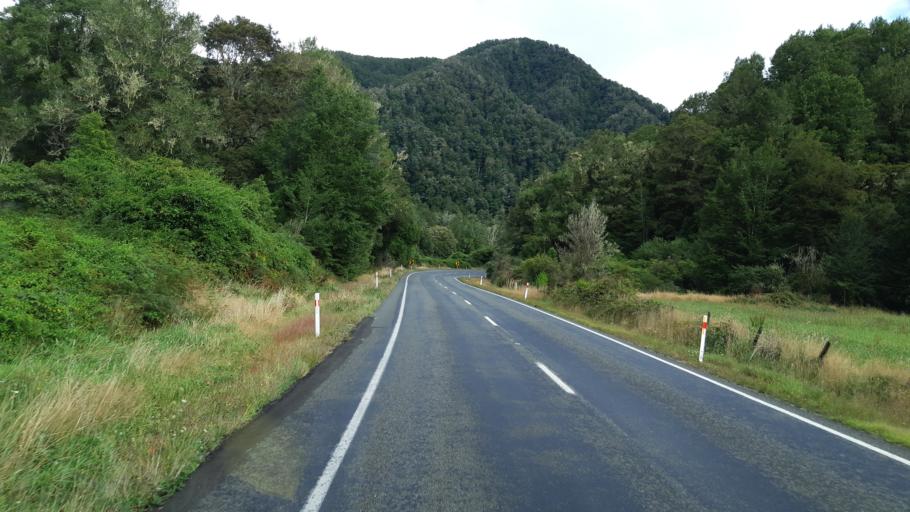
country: NZ
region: West Coast
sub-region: Buller District
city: Westport
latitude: -41.8402
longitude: 172.2464
